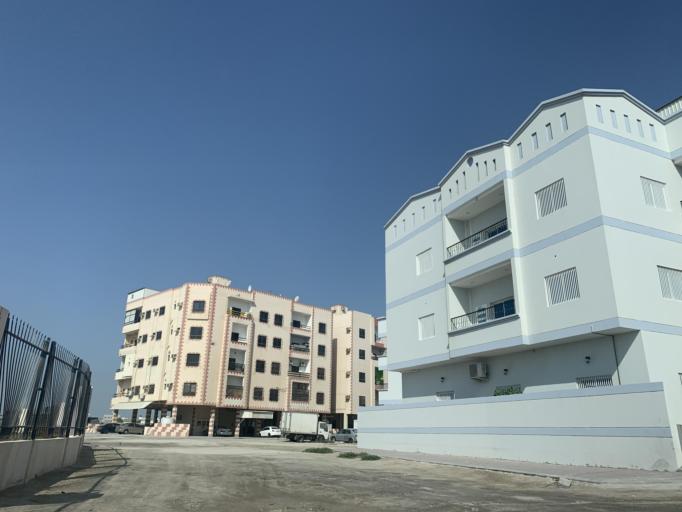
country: BH
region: Central Governorate
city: Madinat Hamad
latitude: 26.1352
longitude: 50.4872
